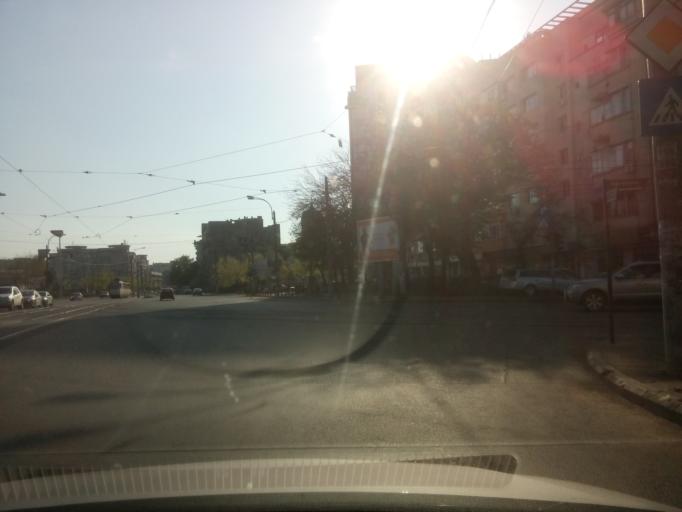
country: RO
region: Bucuresti
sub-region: Municipiul Bucuresti
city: Bucharest
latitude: 44.4329
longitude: 26.1121
